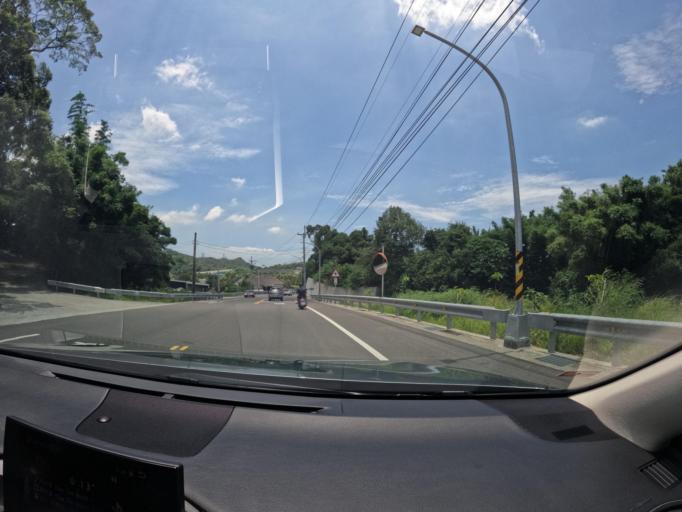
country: TW
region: Taiwan
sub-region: Hsinchu
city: Hsinchu
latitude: 24.6732
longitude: 120.9522
